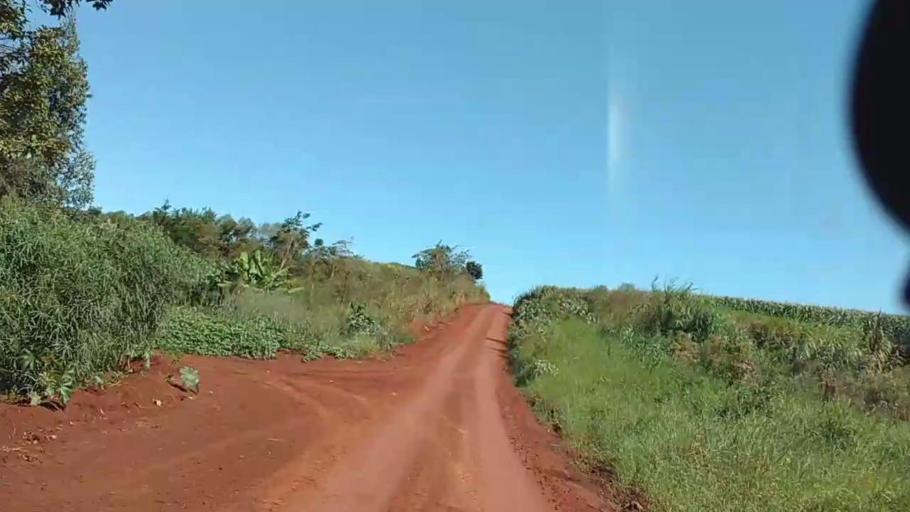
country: PY
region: Alto Parana
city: Naranjal
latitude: -25.9472
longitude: -55.1045
